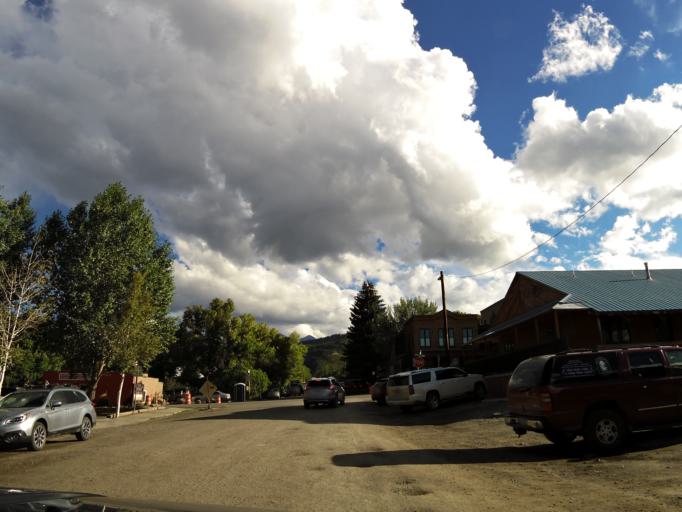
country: US
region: Colorado
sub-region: Ouray County
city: Ouray
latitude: 38.1518
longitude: -107.7577
